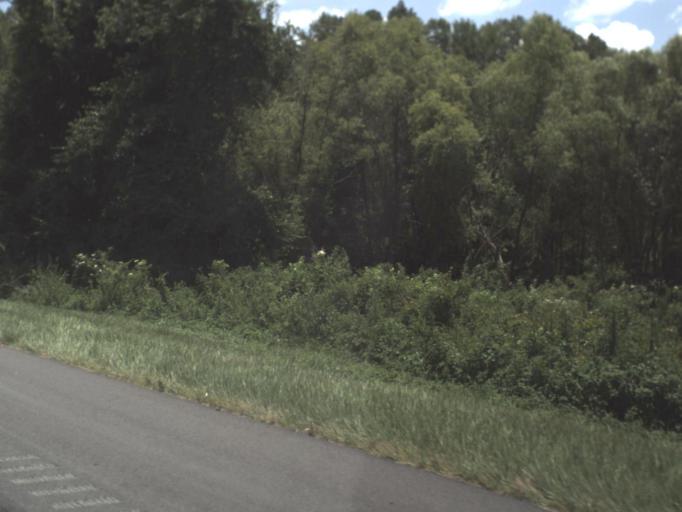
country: US
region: Florida
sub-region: Madison County
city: Madison
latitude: 30.4353
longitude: -83.4783
